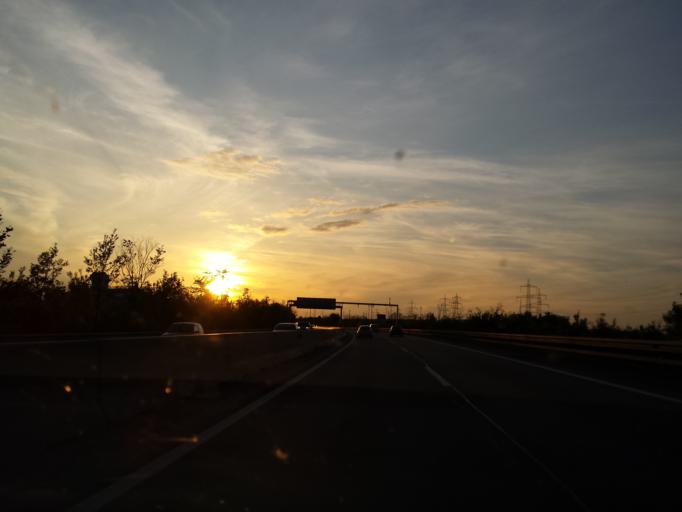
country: AT
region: Lower Austria
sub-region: Politischer Bezirk Bruck an der Leitha
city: Rohrau
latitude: 48.0319
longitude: 16.8273
